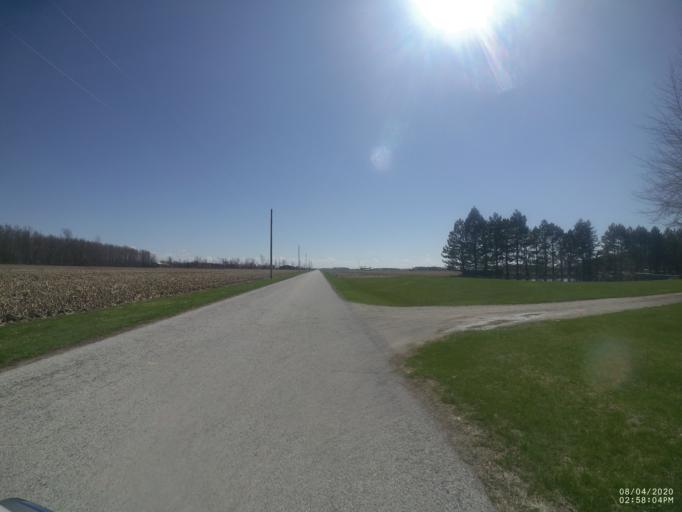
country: US
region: Ohio
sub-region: Sandusky County
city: Gibsonburg
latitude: 41.3293
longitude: -83.2542
